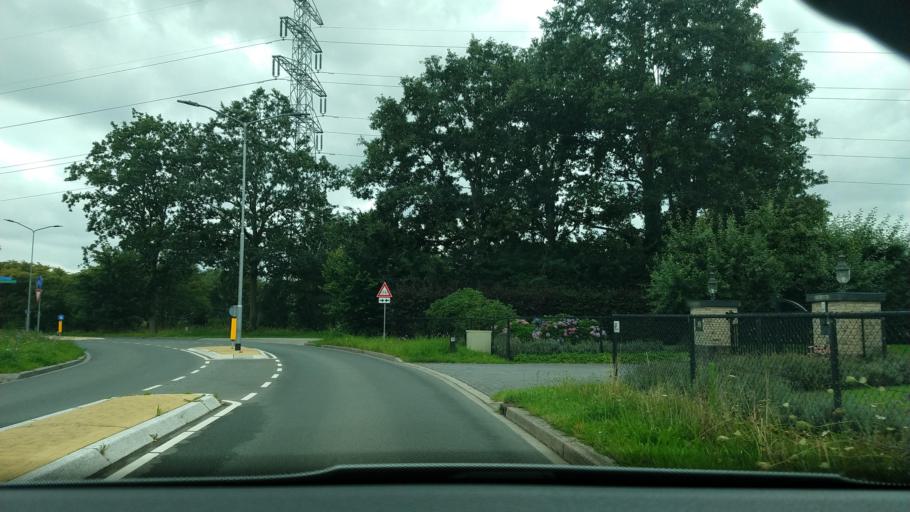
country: NL
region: Gelderland
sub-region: Gemeente Ermelo
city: Horst
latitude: 52.3020
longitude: 5.5994
